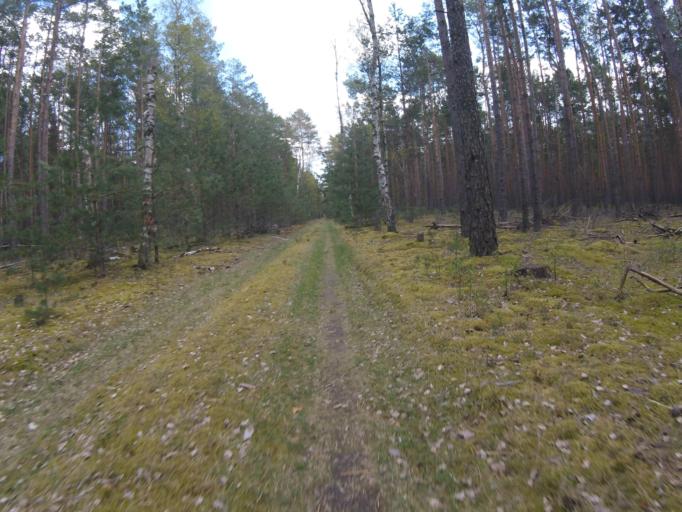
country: DE
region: Brandenburg
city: Halbe
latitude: 52.1832
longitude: 13.7483
